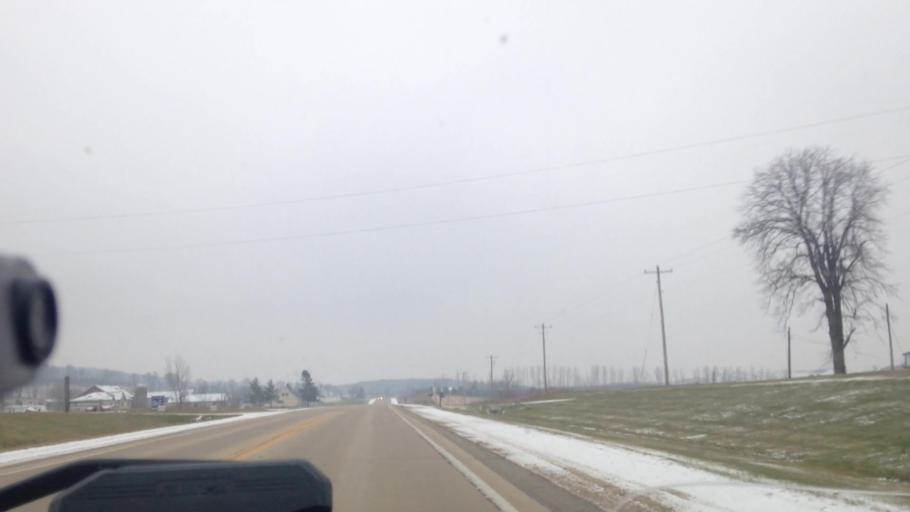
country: US
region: Wisconsin
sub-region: Dodge County
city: Mayville
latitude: 43.4759
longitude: -88.5463
